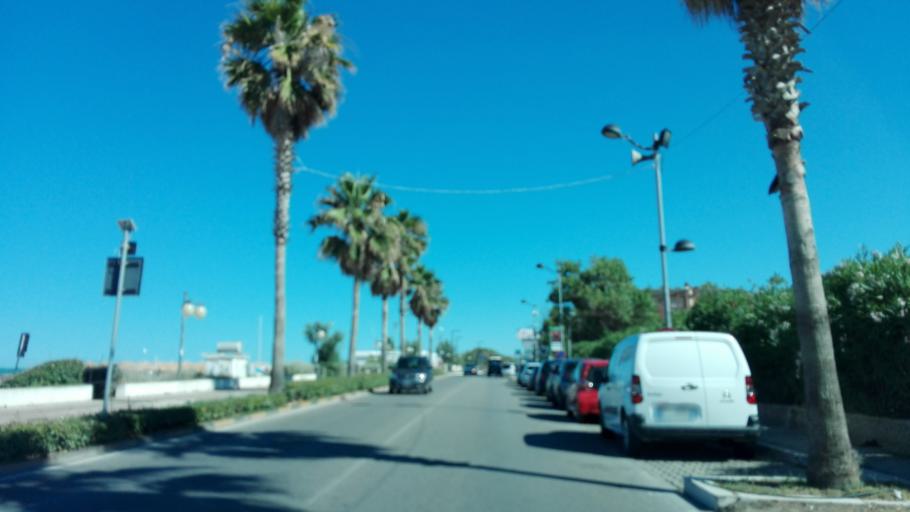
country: IT
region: Abruzzo
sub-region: Provincia di Pescara
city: Montesilvano Marina
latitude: 42.5108
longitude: 14.1681
